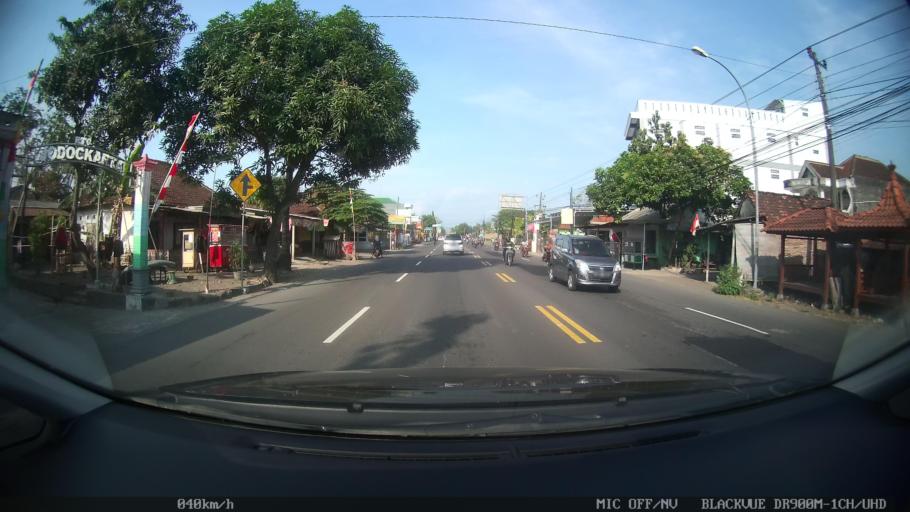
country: ID
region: Daerah Istimewa Yogyakarta
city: Pandak
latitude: -7.9062
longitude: 110.3126
